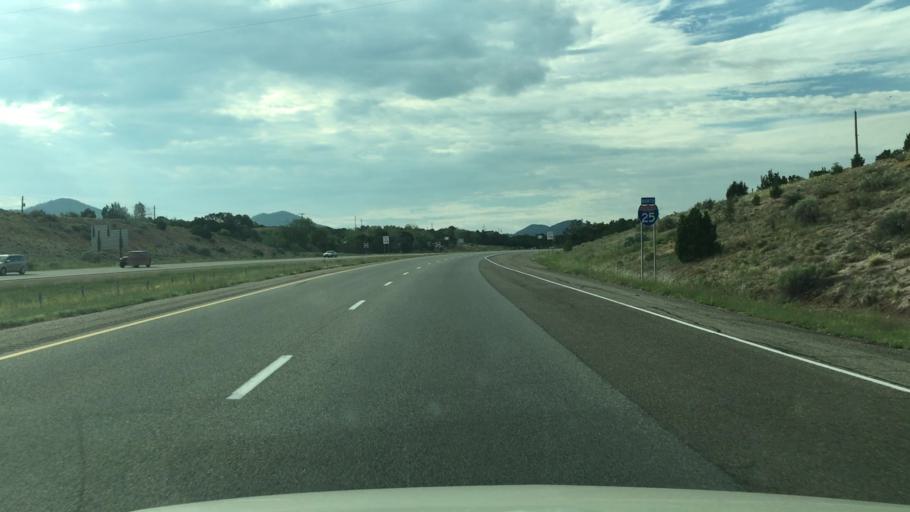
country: US
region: New Mexico
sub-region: Santa Fe County
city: Santa Fe
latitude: 35.6344
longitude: -105.9275
